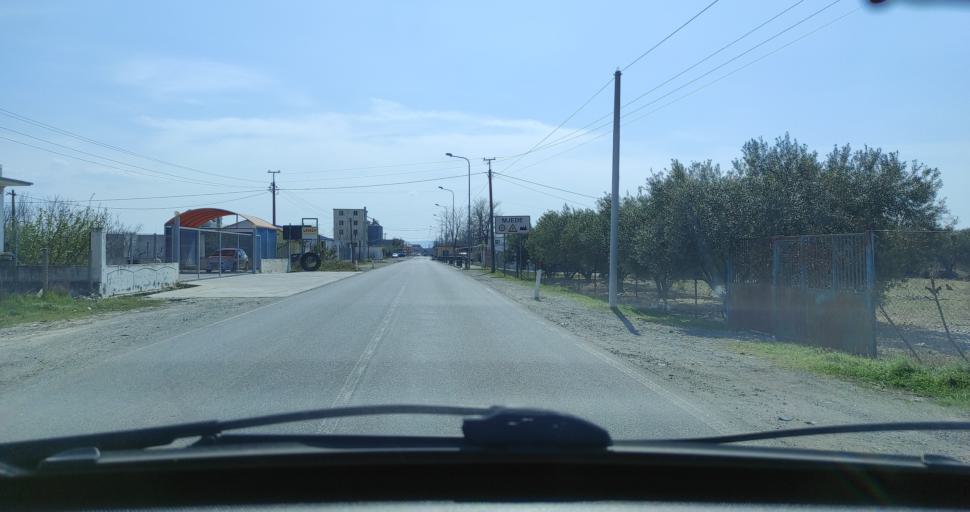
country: AL
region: Shkoder
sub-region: Rrethi i Shkodres
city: Vau i Dejes
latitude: 42.0056
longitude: 19.6181
